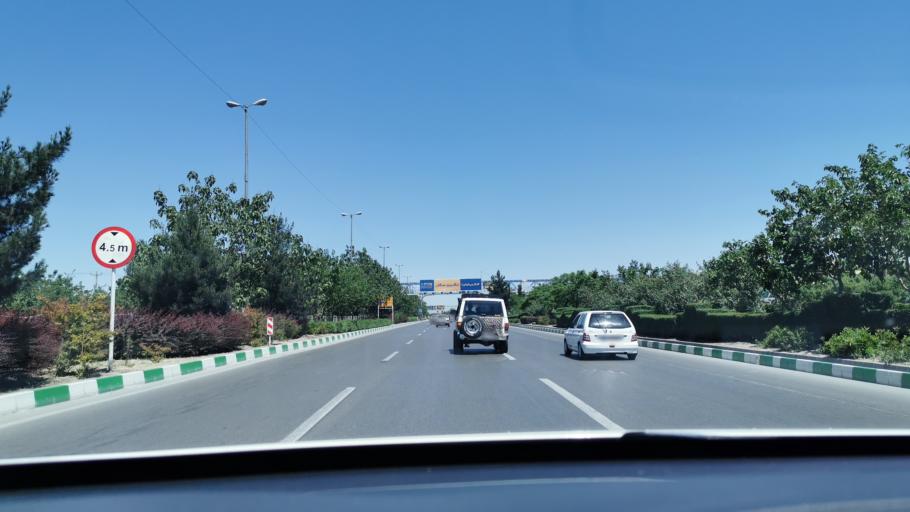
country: IR
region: Razavi Khorasan
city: Mashhad
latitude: 36.2587
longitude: 59.6372
